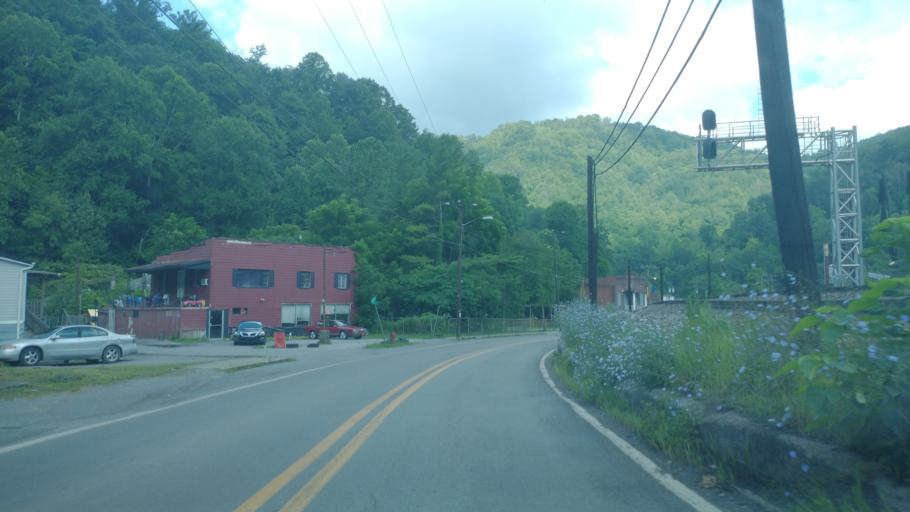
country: US
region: West Virginia
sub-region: McDowell County
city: Welch
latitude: 37.4154
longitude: -81.4461
